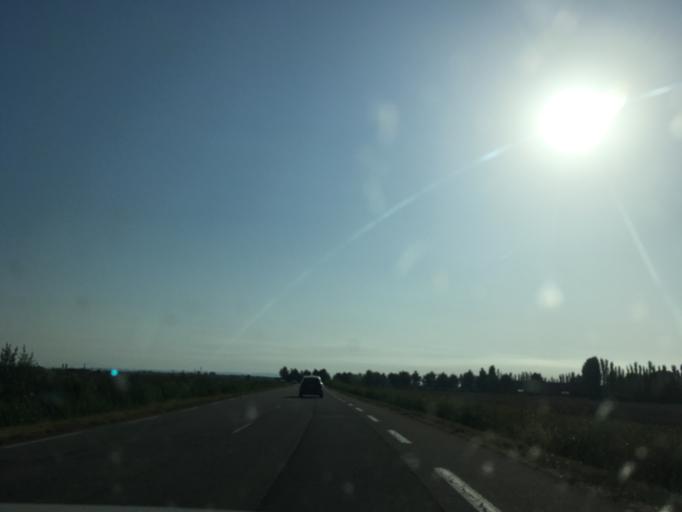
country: FR
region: Languedoc-Roussillon
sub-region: Departement du Gard
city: Fourques
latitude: 43.6339
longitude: 4.5456
